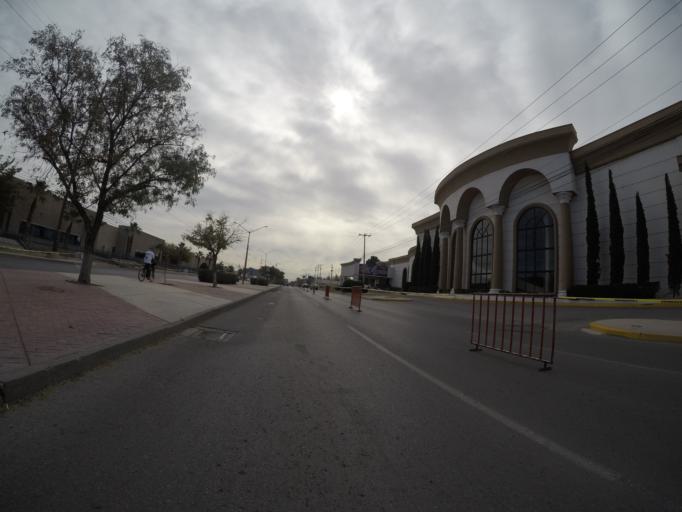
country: MX
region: Chihuahua
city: Ciudad Juarez
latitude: 31.7216
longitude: -106.3992
